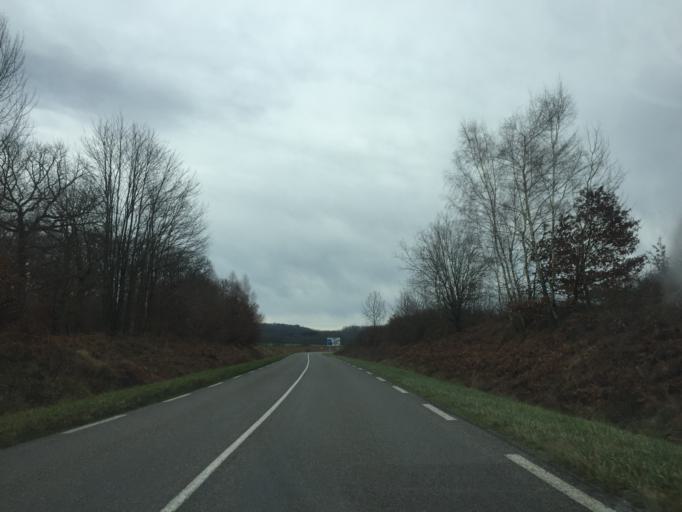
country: FR
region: Franche-Comte
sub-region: Departement du Jura
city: Poligny
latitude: 46.8406
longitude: 5.5644
